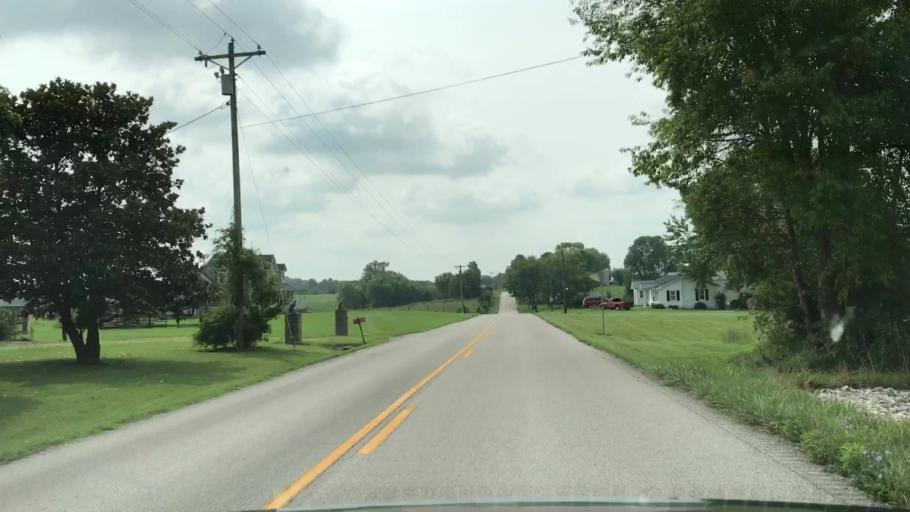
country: US
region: Kentucky
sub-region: Edmonson County
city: Brownsville
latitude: 37.1118
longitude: -86.1487
